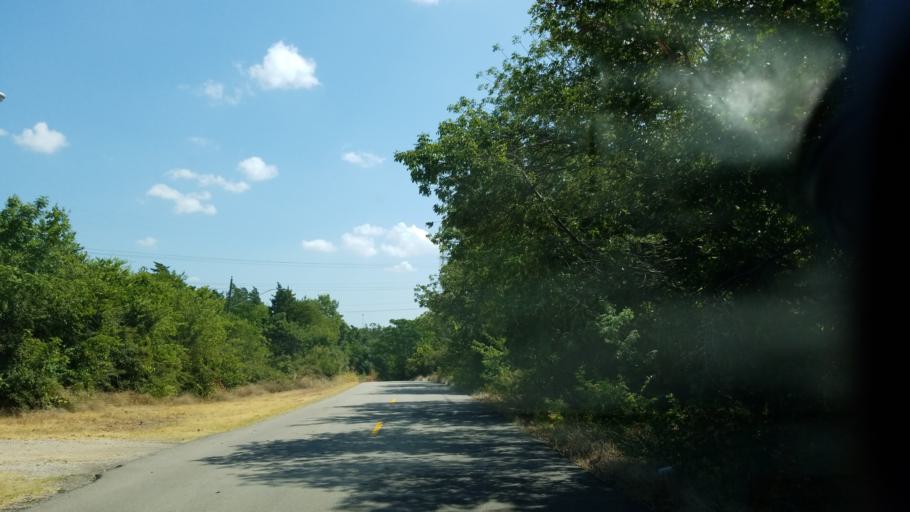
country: US
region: Texas
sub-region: Dallas County
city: Cockrell Hill
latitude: 32.7114
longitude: -96.9186
